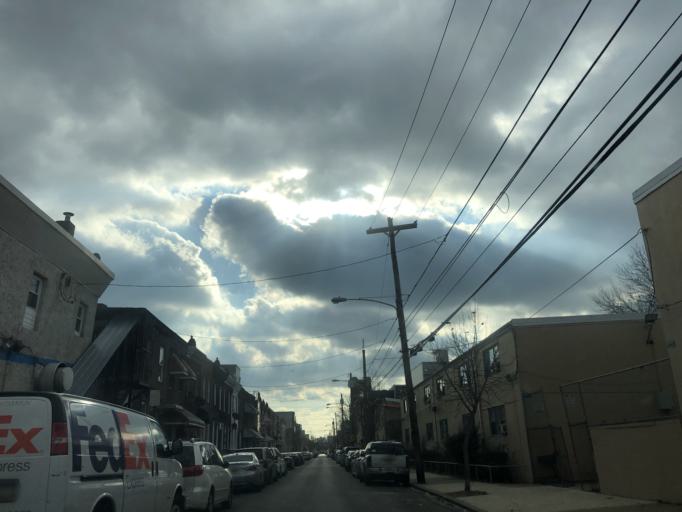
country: US
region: Pennsylvania
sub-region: Philadelphia County
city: Philadelphia
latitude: 39.9332
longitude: -75.1796
